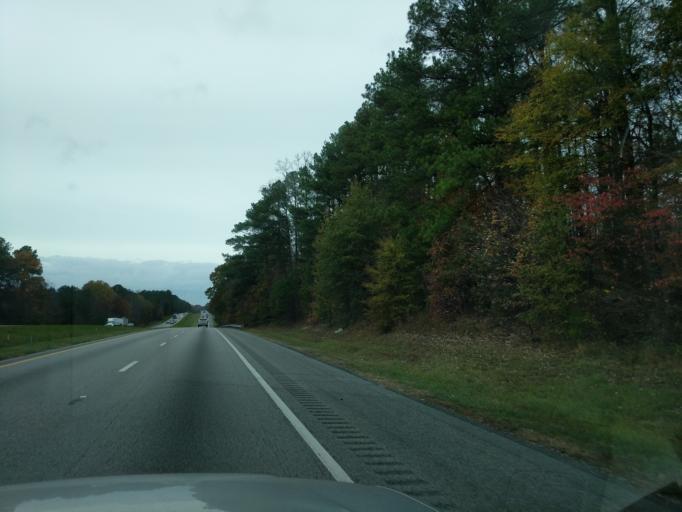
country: US
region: South Carolina
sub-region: Laurens County
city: Joanna
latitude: 34.4475
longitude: -81.7746
